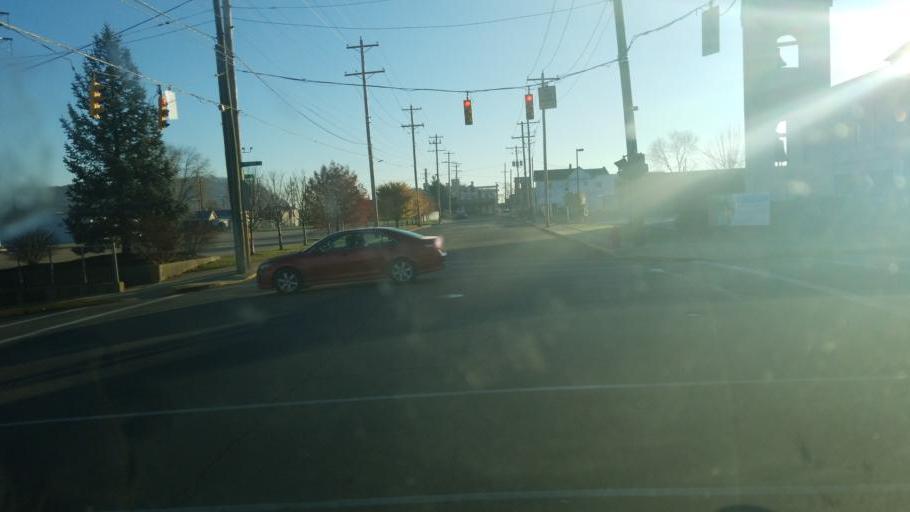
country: US
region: Ohio
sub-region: Scioto County
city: Portsmouth
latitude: 38.7370
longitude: -82.9856
